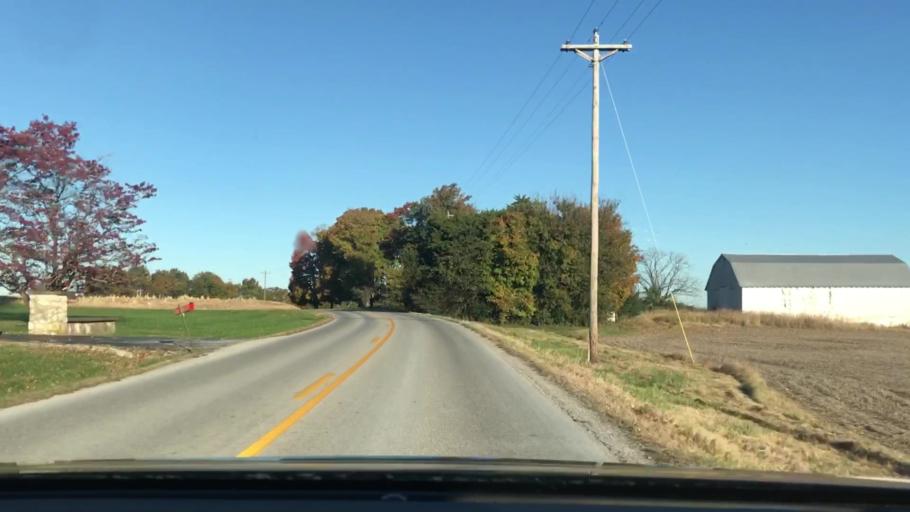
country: US
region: Kentucky
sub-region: Logan County
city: Auburn
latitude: 36.8448
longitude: -86.6973
